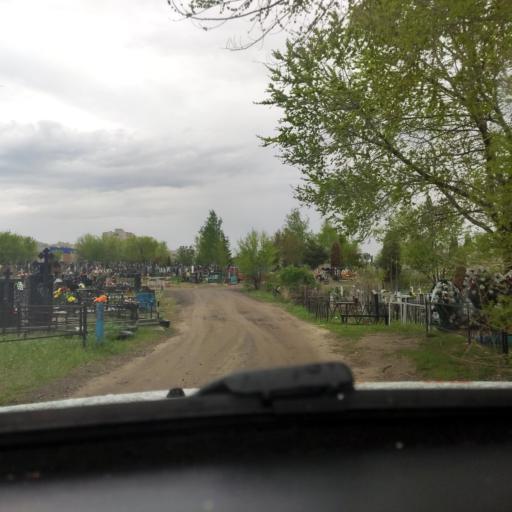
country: RU
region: Voronezj
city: Somovo
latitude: 51.6647
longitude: 39.2929
